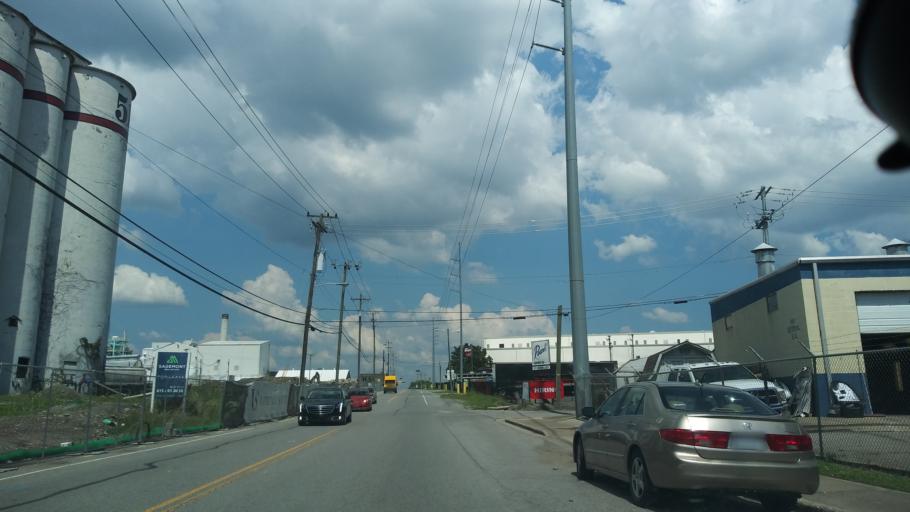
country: US
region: Tennessee
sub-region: Davidson County
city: Nashville
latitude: 36.1624
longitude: -86.8471
